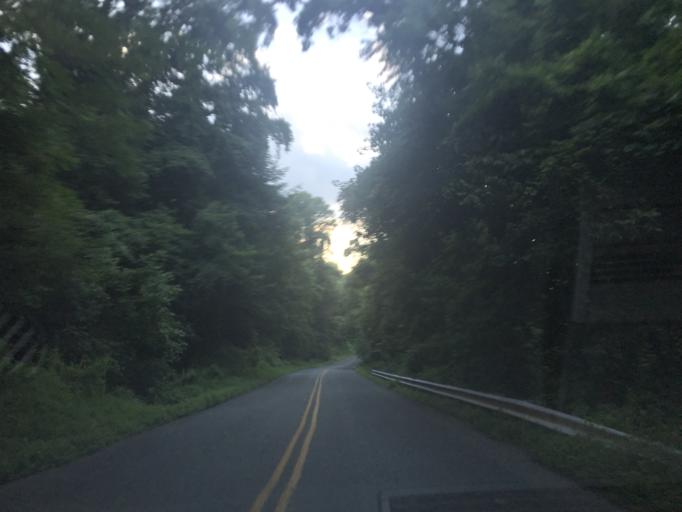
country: US
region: Maryland
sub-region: Cecil County
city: Rising Sun
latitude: 39.6524
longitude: -76.1772
